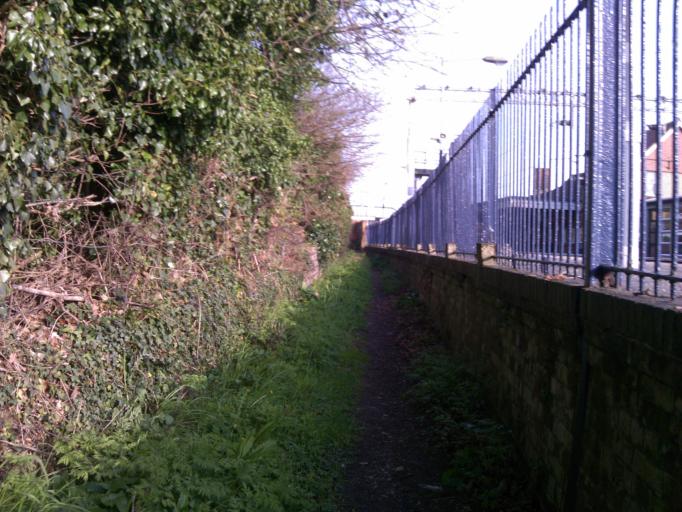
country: GB
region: England
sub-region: Essex
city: Wivenhoe
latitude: 51.8570
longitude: 0.9554
